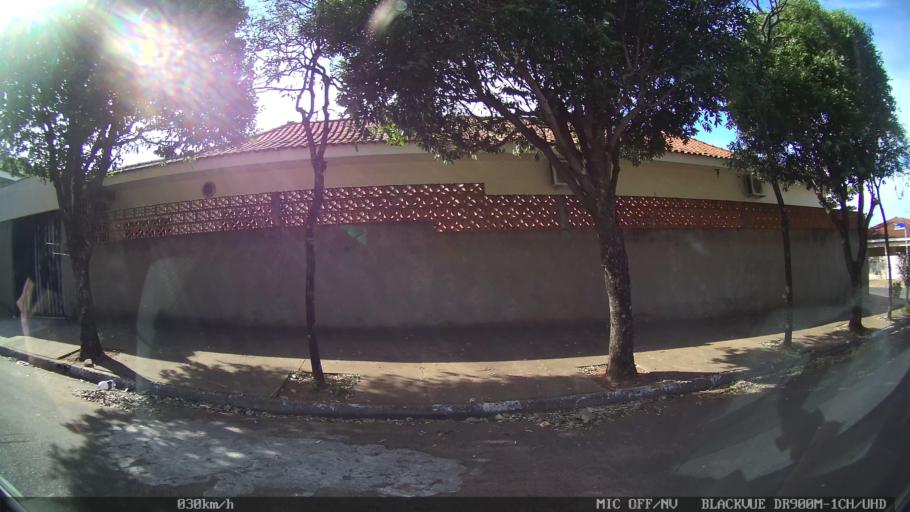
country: BR
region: Sao Paulo
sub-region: Catanduva
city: Catanduva
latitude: -21.1156
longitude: -48.9680
